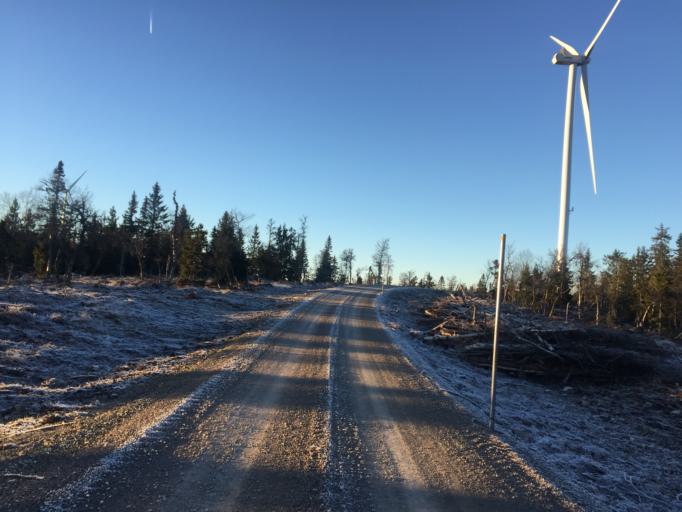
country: NO
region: Hedmark
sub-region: Elverum
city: Elverum
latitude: 61.2120
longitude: 11.7817
